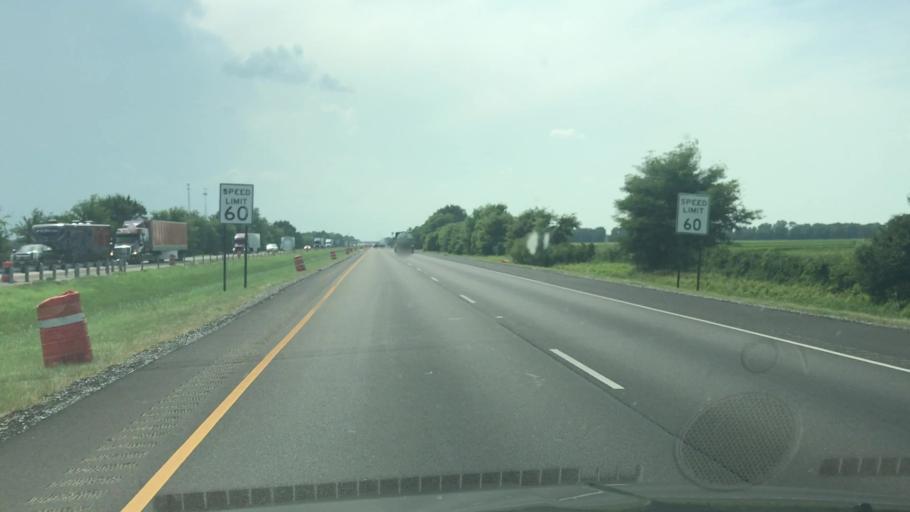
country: US
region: Arkansas
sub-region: Crittenden County
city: Earle
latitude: 35.1334
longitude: -90.4677
